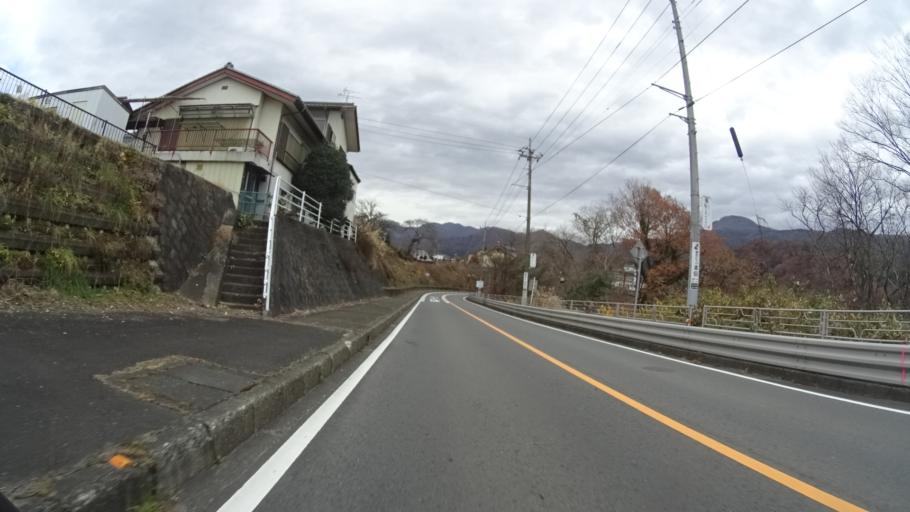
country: JP
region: Gunma
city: Nakanojomachi
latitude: 36.7266
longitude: 138.8889
